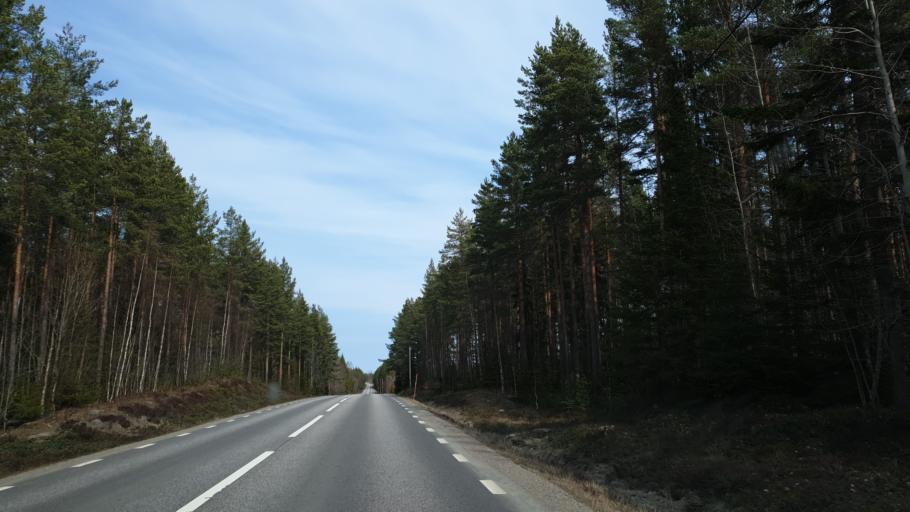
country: SE
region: Gaevleborg
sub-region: Gavle Kommun
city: Norrsundet
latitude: 61.0078
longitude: 17.1317
